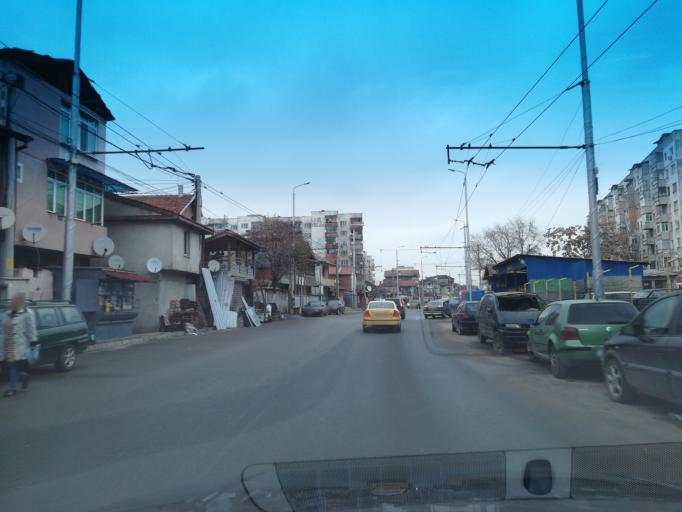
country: BG
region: Plovdiv
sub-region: Obshtina Plovdiv
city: Plovdiv
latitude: 42.1546
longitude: 24.7872
